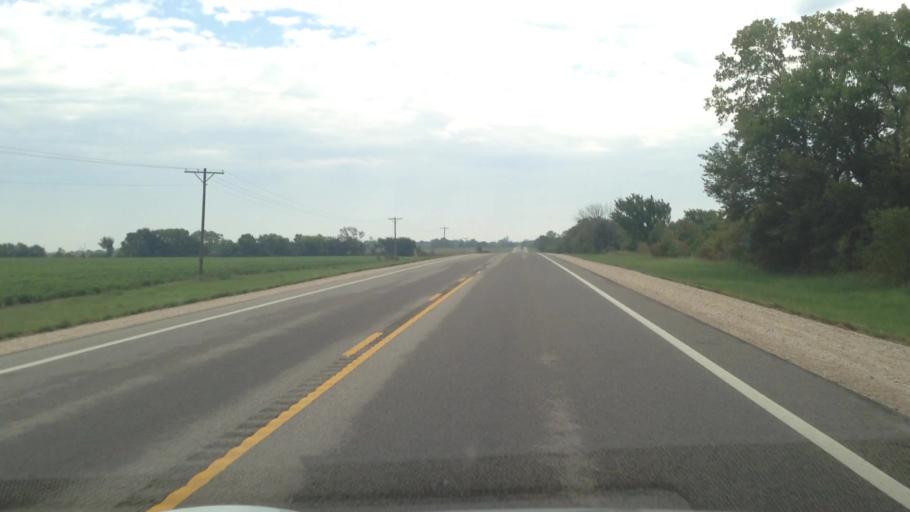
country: US
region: Kansas
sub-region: Allen County
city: Iola
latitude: 37.9053
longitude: -95.0947
